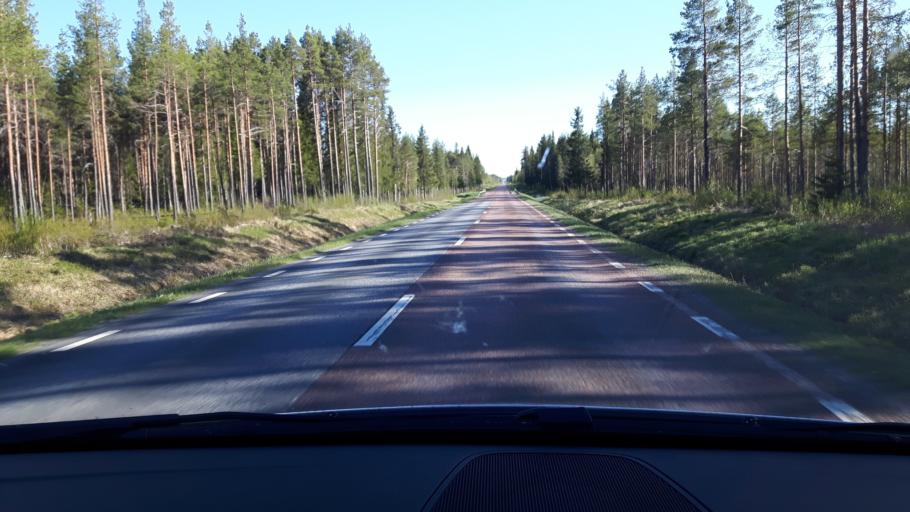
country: SE
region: Jaemtland
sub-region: Stroemsunds Kommun
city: Stroemsund
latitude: 63.8061
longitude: 15.5192
